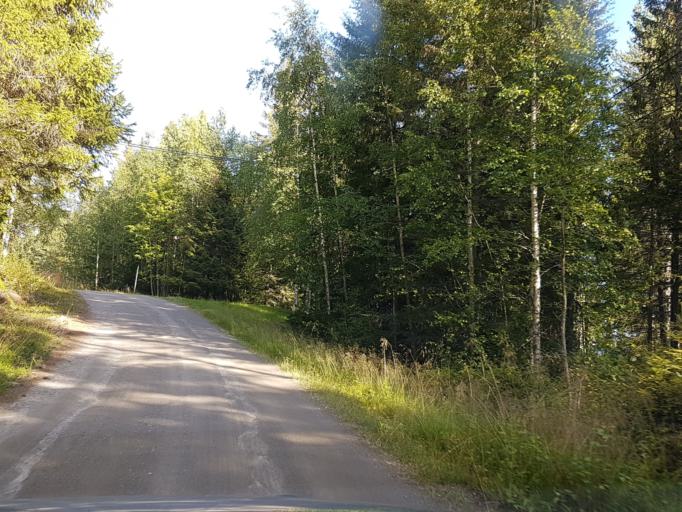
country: SE
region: Vaesterbotten
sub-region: Robertsfors Kommun
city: Robertsfors
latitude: 64.0453
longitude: 20.9032
